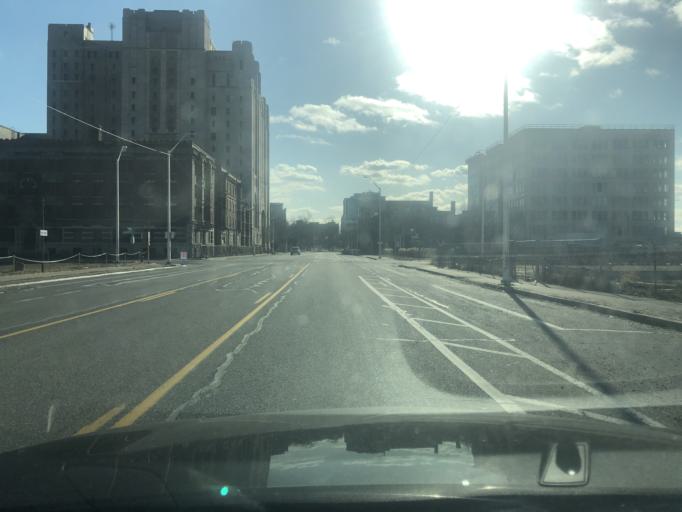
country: US
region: Michigan
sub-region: Wayne County
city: Detroit
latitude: 42.3430
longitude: -83.0619
